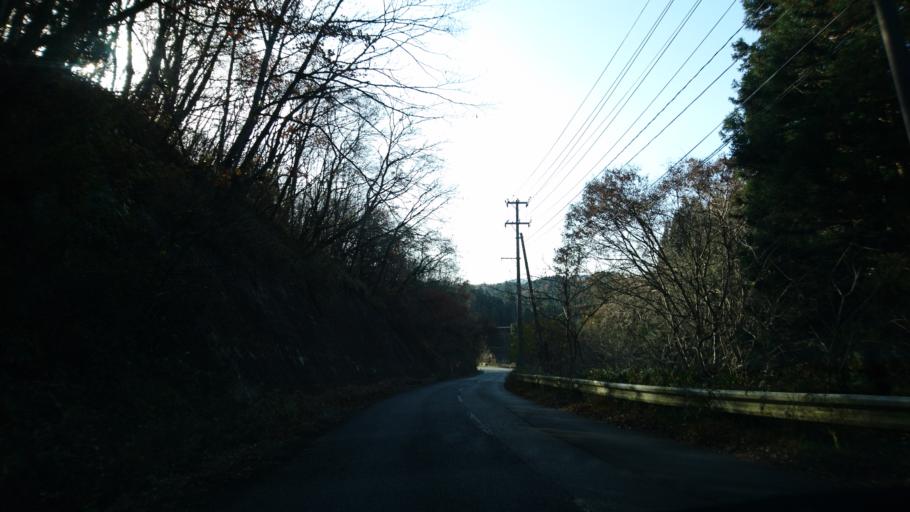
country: JP
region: Iwate
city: Ichinoseki
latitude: 38.8658
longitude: 141.3289
